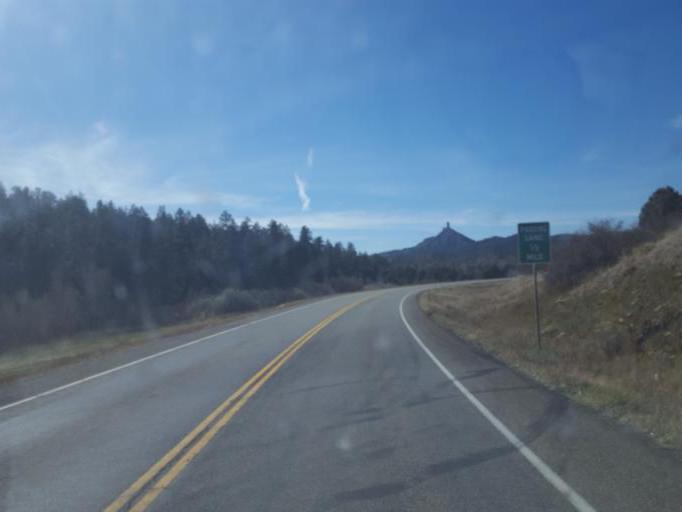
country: US
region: Colorado
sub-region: Archuleta County
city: Pagosa Springs
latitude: 37.2099
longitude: -107.2408
